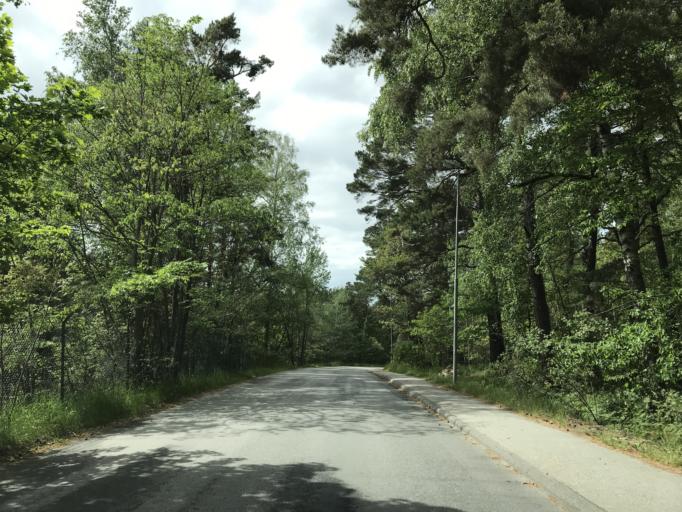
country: SE
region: Stockholm
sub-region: Solna Kommun
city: Solna
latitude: 59.3857
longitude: 18.0068
